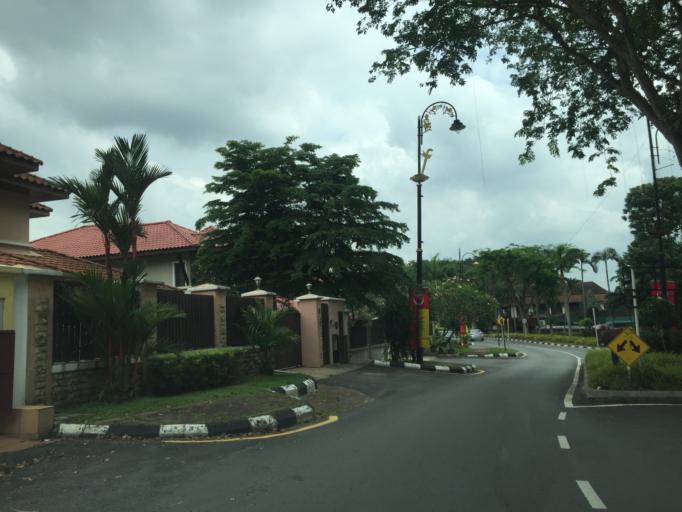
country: MY
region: Selangor
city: Klang
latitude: 3.0374
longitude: 101.4477
